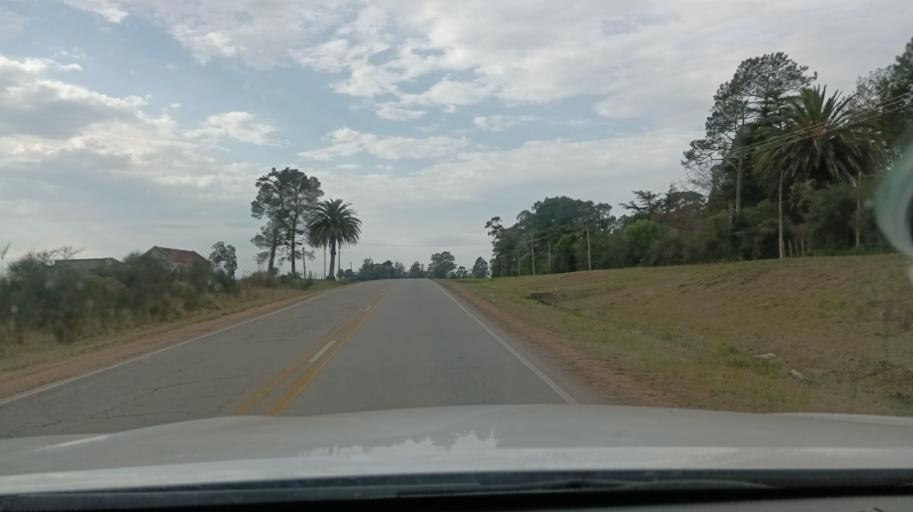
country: UY
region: Canelones
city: Toledo
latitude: -34.7093
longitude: -56.1086
